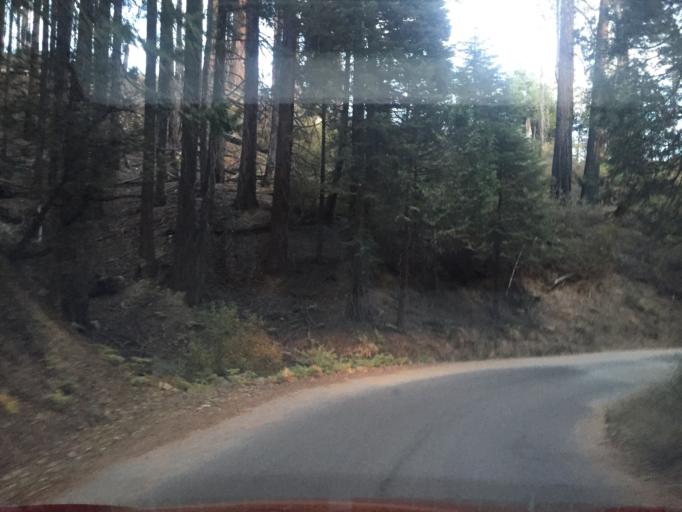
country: US
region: California
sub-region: Tulare County
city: Three Rivers
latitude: 36.4561
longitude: -118.6870
